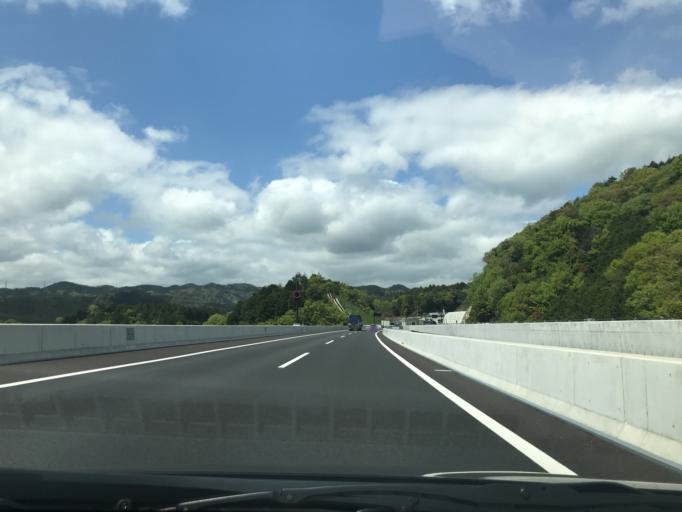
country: JP
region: Osaka
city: Takatsuki
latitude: 34.8899
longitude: 135.6113
